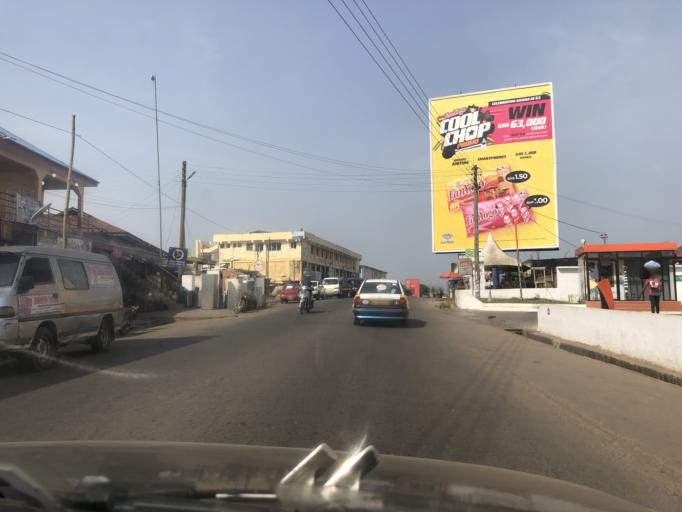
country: GH
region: Eastern
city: Koforidua
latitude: 6.0969
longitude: -0.2552
